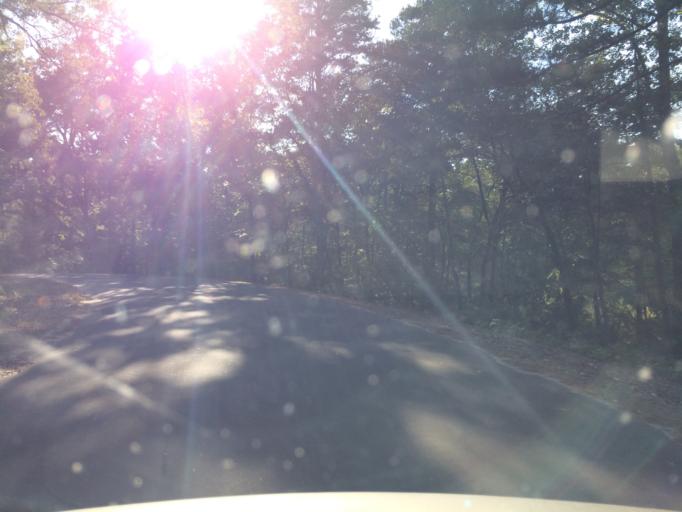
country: US
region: Texas
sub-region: Wood County
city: Hawkins
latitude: 32.6299
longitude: -95.2592
